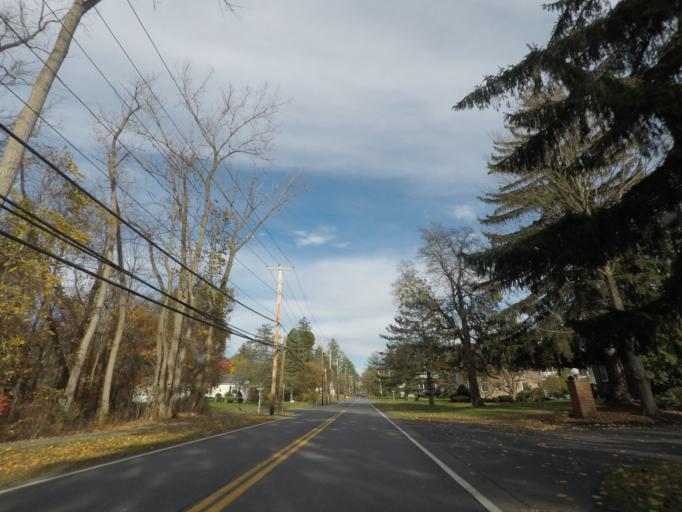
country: US
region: New York
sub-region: Albany County
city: Delmar
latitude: 42.6160
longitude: -73.8499
